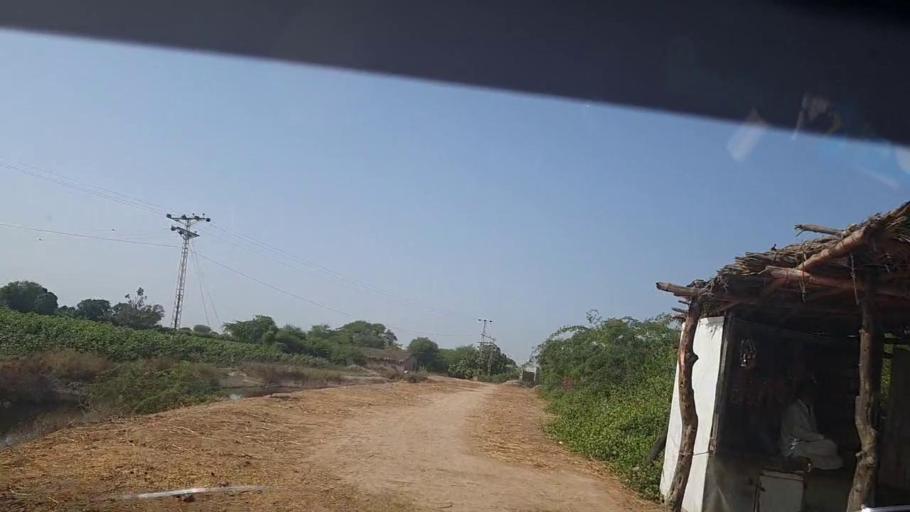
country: PK
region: Sindh
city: Rajo Khanani
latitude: 24.9578
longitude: 68.8981
